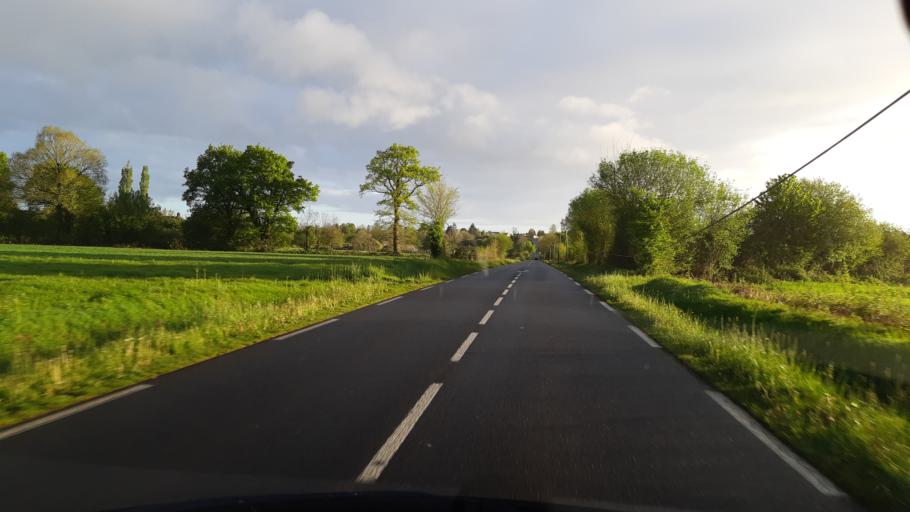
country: FR
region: Lower Normandy
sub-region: Departement de la Manche
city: Tessy-sur-Vire
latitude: 49.0168
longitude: -1.1482
